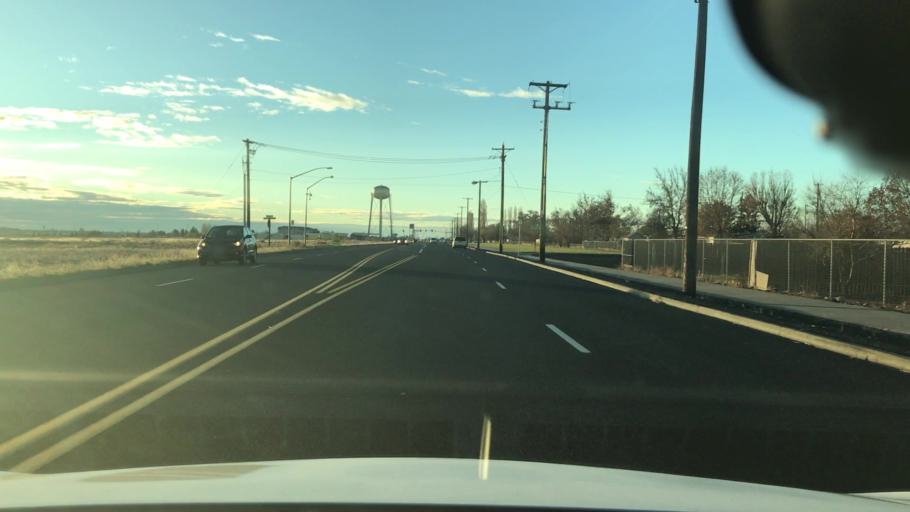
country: US
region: Washington
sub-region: Grant County
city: Moses Lake North
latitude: 47.1681
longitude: -119.3161
